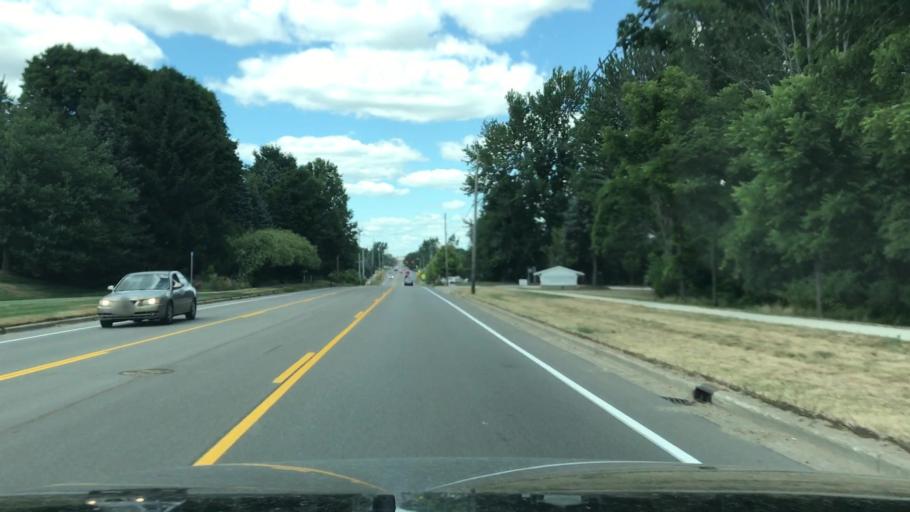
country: US
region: Michigan
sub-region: Kent County
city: Byron Center
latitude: 42.8223
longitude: -85.7230
